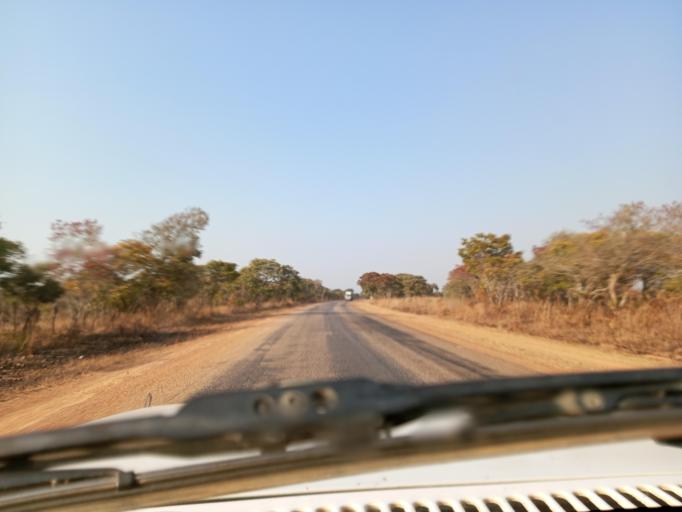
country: ZM
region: Northern
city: Mpika
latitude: -12.3683
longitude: 31.1032
